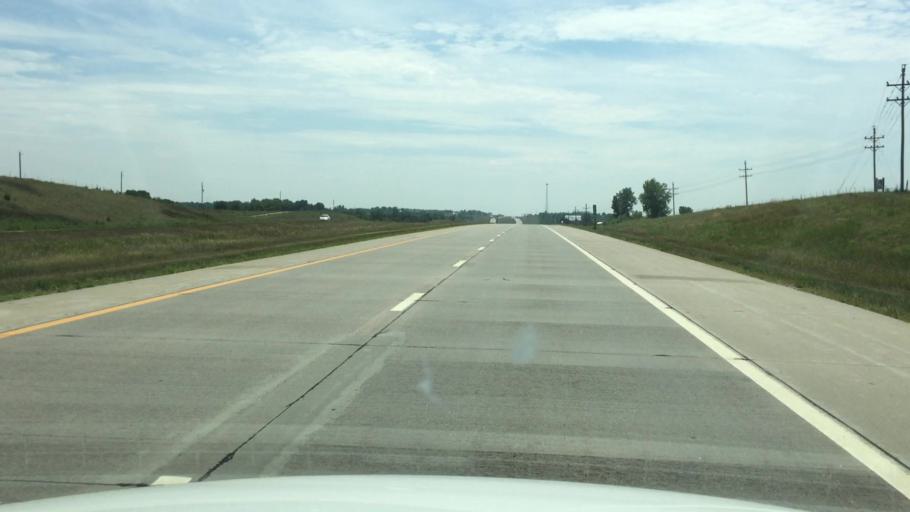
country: US
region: Kansas
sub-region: Jackson County
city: Holton
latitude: 39.2681
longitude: -95.7199
